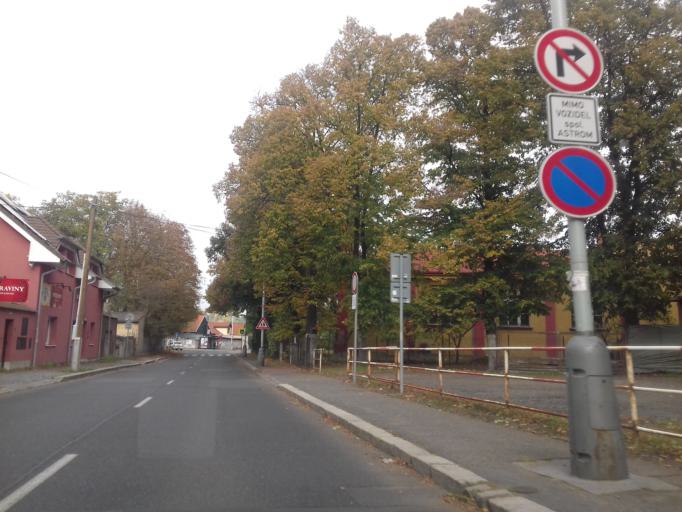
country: CZ
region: Praha
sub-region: Praha 12
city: Modrany
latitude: 50.0214
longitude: 14.4052
